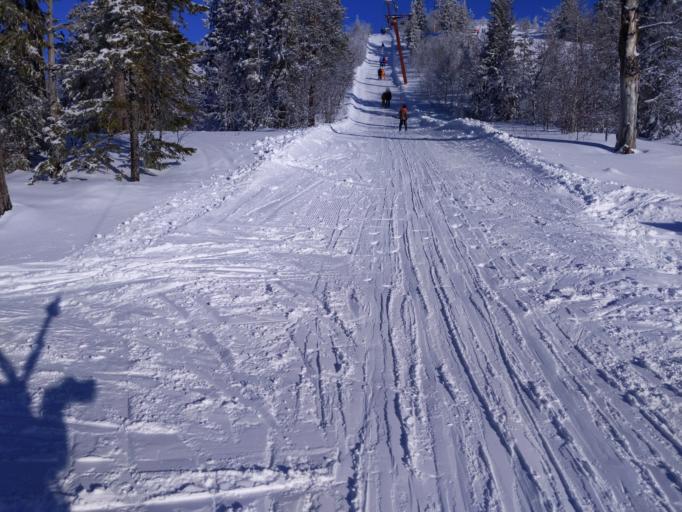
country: SE
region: Jaemtland
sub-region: Harjedalens Kommun
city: Sveg
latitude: 62.4315
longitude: 13.9600
